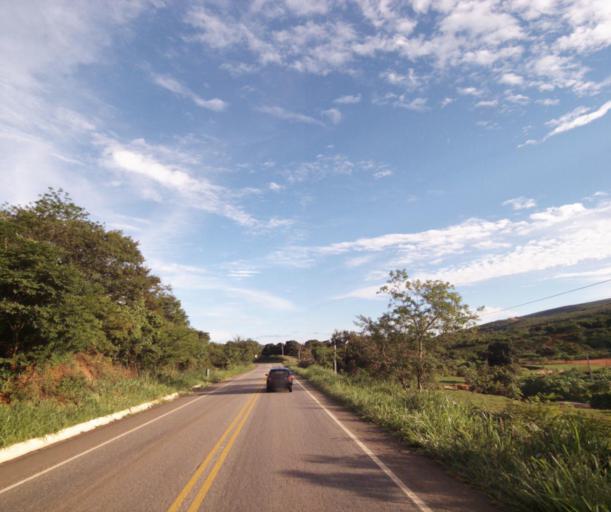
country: BR
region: Bahia
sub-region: Caetite
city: Caetite
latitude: -14.0786
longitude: -42.4561
